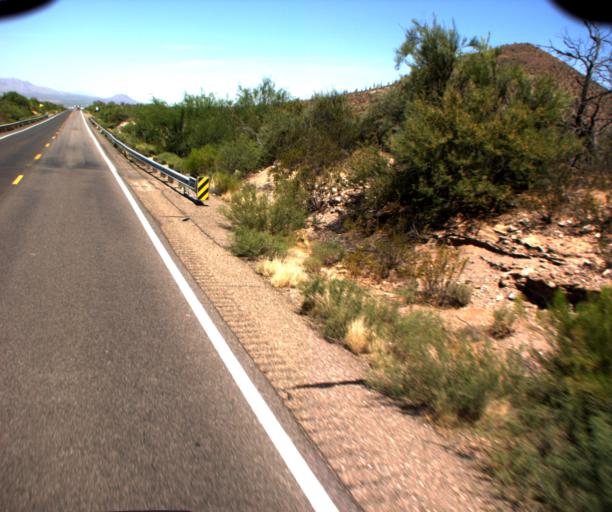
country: US
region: Arizona
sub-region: Gila County
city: Peridot
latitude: 33.2881
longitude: -110.3934
